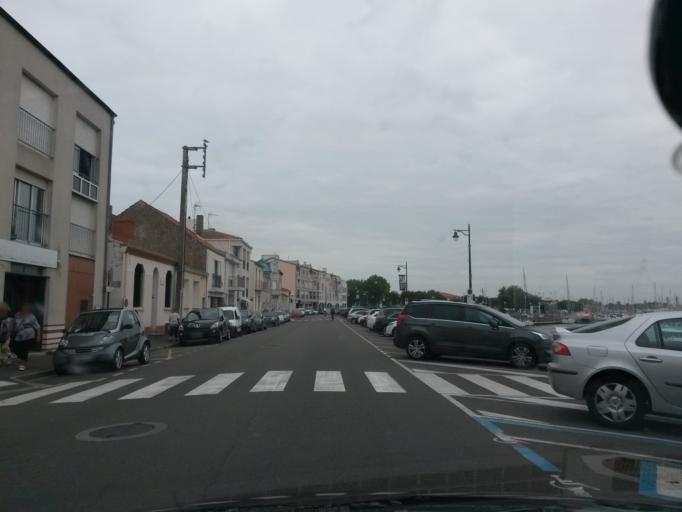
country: FR
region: Pays de la Loire
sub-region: Departement de la Vendee
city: Les Sables-d'Olonne
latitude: 46.4982
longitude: -1.7968
